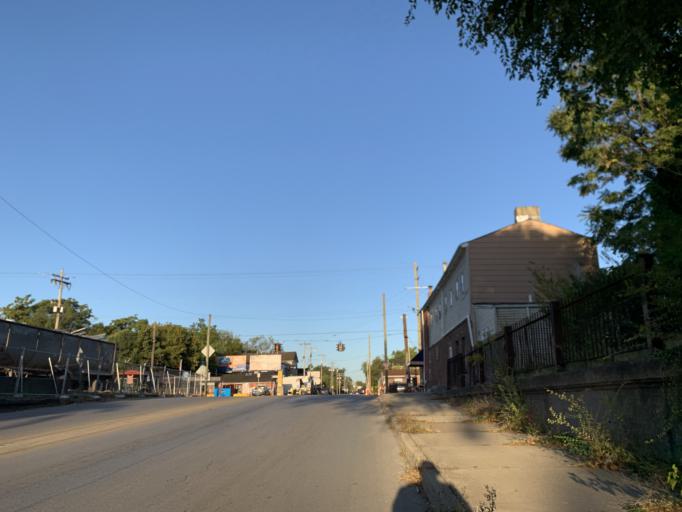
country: US
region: Kentucky
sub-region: Jefferson County
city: Louisville
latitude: 38.2366
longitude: -85.7778
